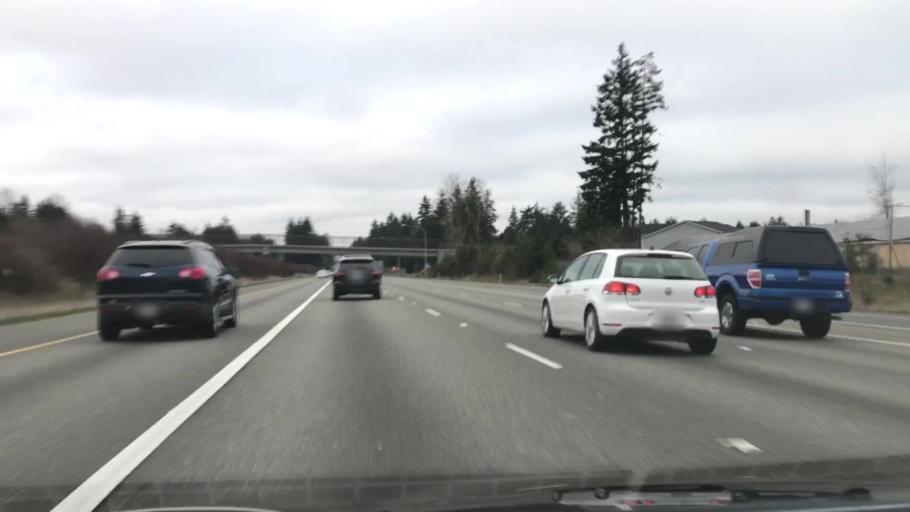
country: US
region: Washington
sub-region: Snohomish County
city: Martha Lake
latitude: 47.8852
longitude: -122.2304
